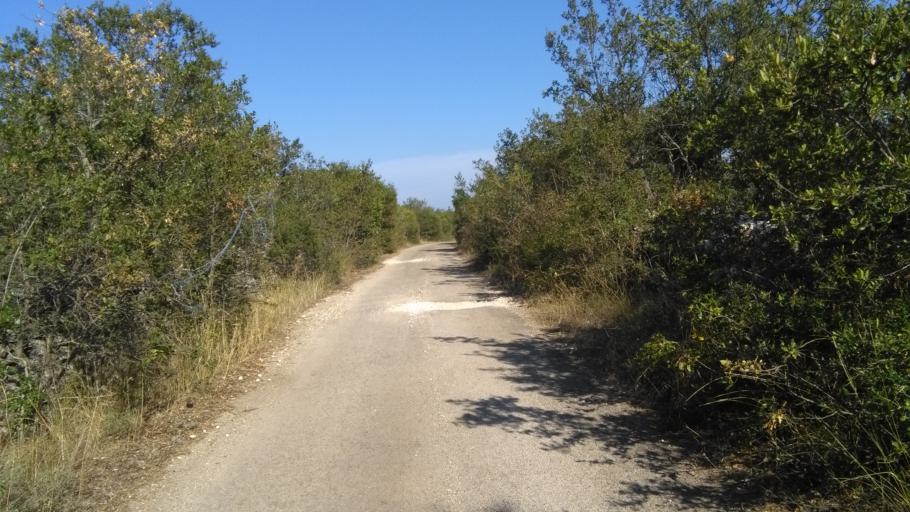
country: IT
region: Apulia
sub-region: Provincia di Bari
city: Putignano
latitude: 40.8204
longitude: 17.0398
